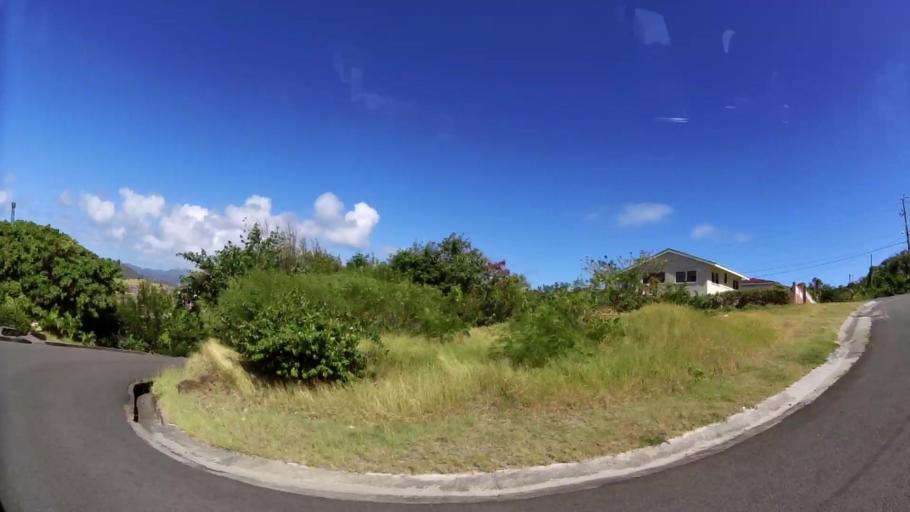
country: LC
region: Vieux-Fort
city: Vieux Fort
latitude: 13.7196
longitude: -60.9510
